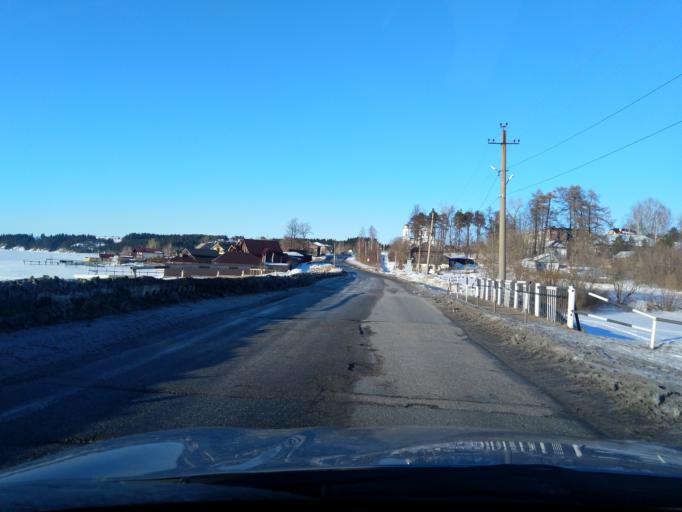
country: RU
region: Perm
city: Polazna
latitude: 58.3047
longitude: 56.4189
